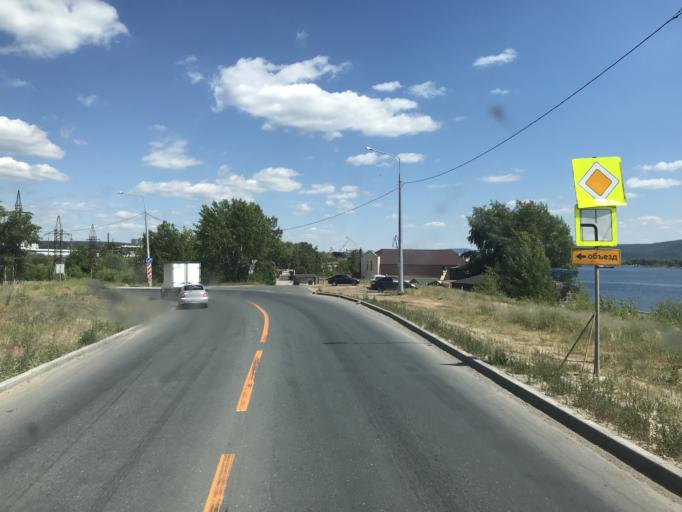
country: RU
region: Samara
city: Zhigulevsk
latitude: 53.4677
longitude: 49.5117
